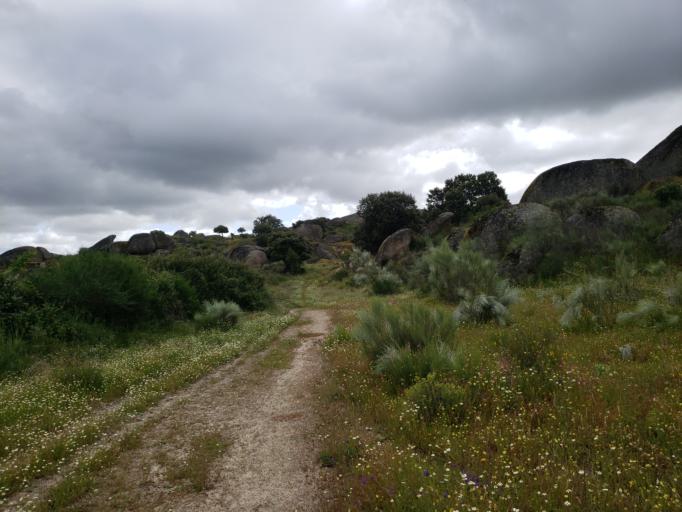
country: ES
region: Extremadura
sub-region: Provincia de Caceres
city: Malpartida de Caceres
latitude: 39.4236
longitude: -6.4958
